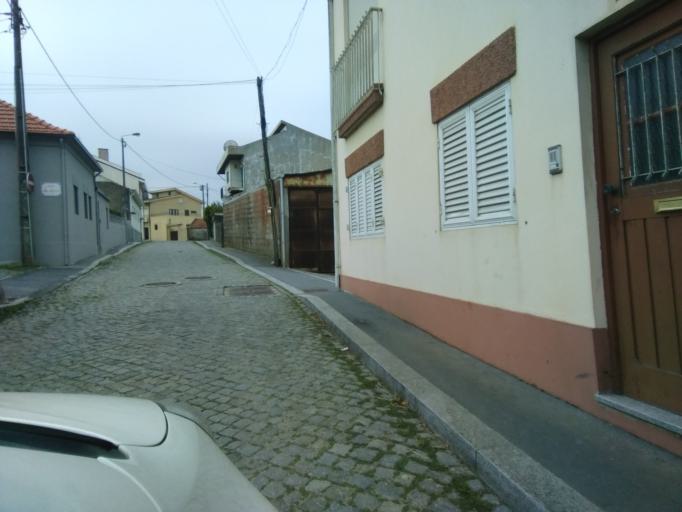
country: PT
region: Porto
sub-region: Matosinhos
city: Lavra
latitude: 41.2336
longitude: -8.7154
